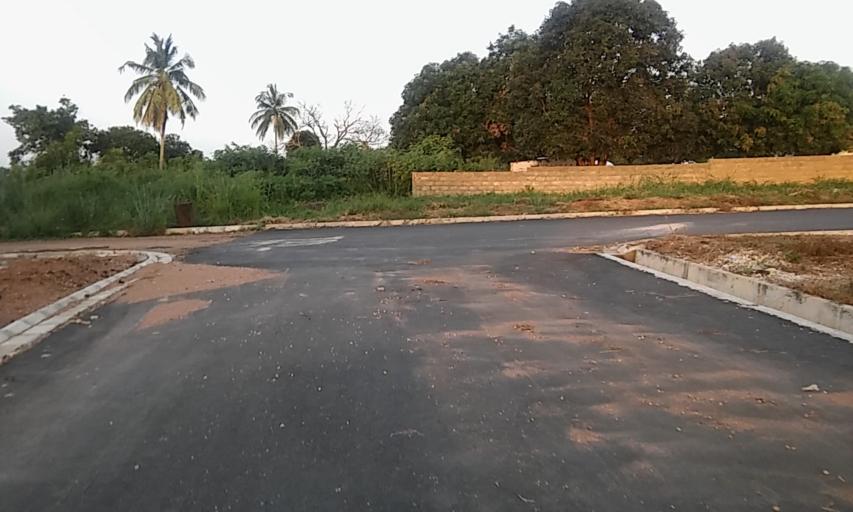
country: CI
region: Vallee du Bandama
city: Bouake
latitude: 7.6910
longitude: -5.0630
